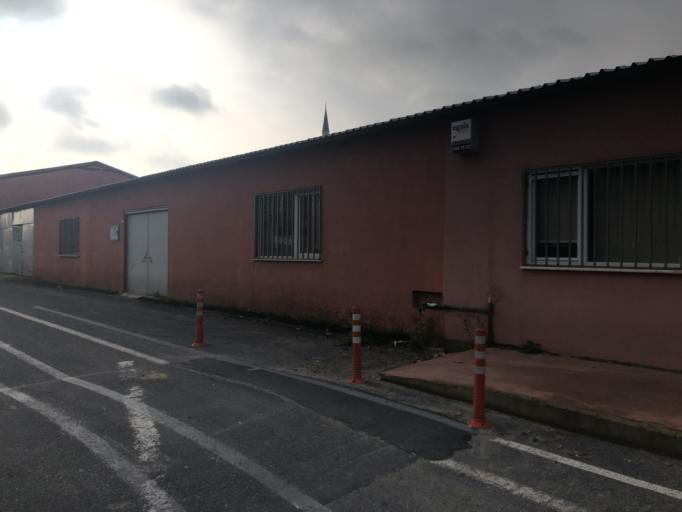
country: TR
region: Istanbul
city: merter keresteciler
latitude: 41.0221
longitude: 28.8865
